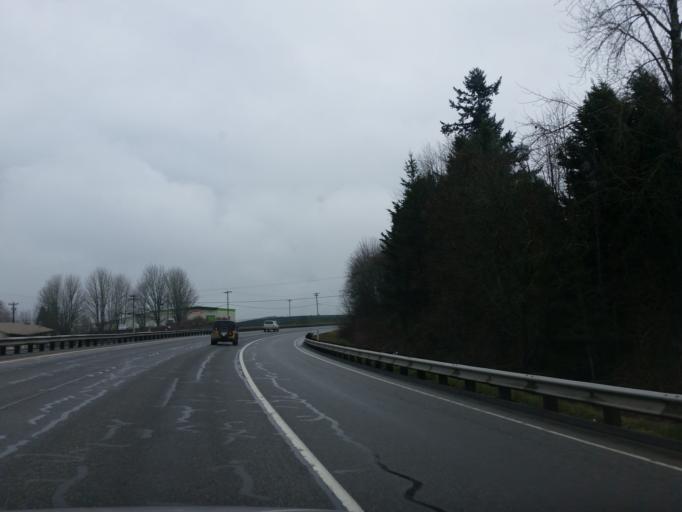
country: US
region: Washington
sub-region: Snohomish County
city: Maltby
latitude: 47.7944
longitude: -122.1348
